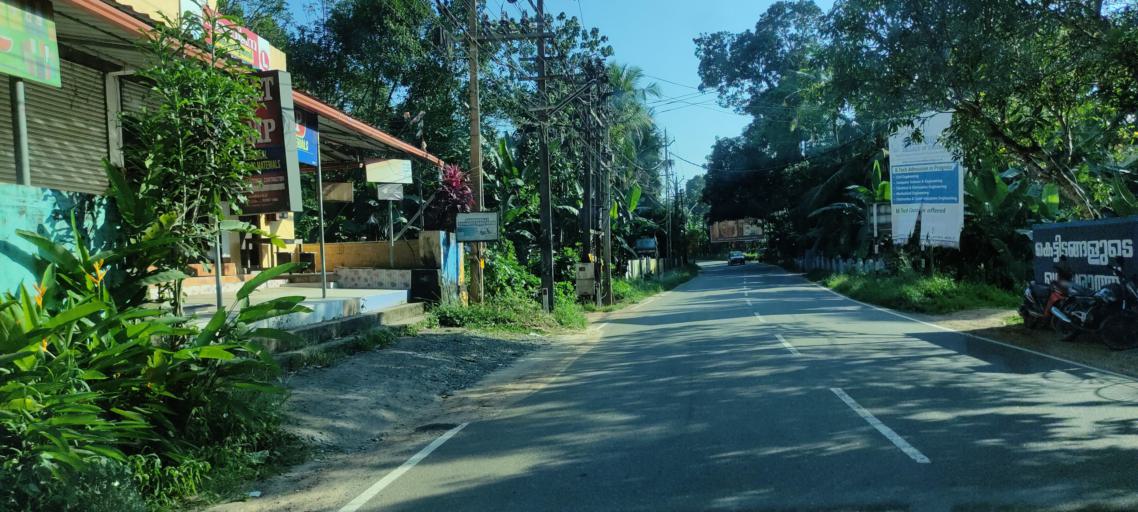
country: IN
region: Kerala
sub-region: Pattanamtitta
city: Adur
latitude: 9.1737
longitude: 76.7416
